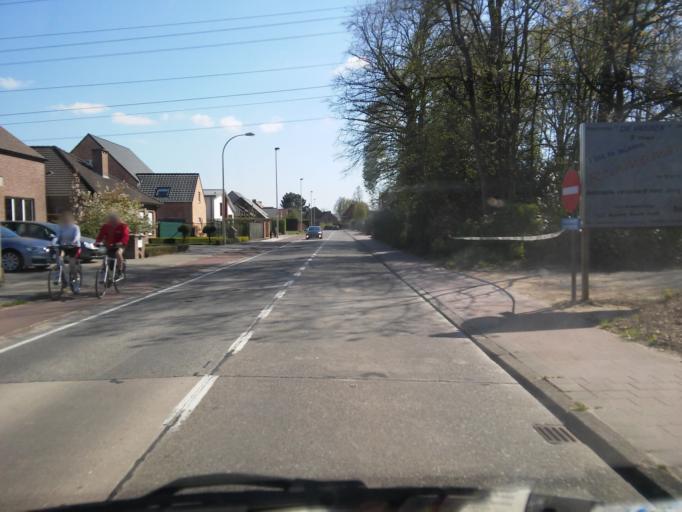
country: BE
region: Flanders
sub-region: Provincie Antwerpen
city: Aartselaar
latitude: 51.1124
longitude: 4.4067
